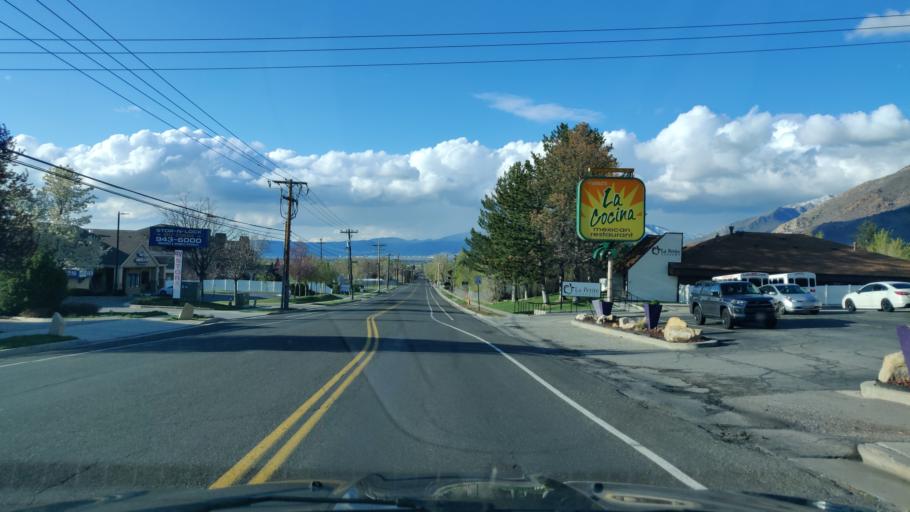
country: US
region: Utah
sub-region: Salt Lake County
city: Cottonwood Heights
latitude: 40.6244
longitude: -111.8247
